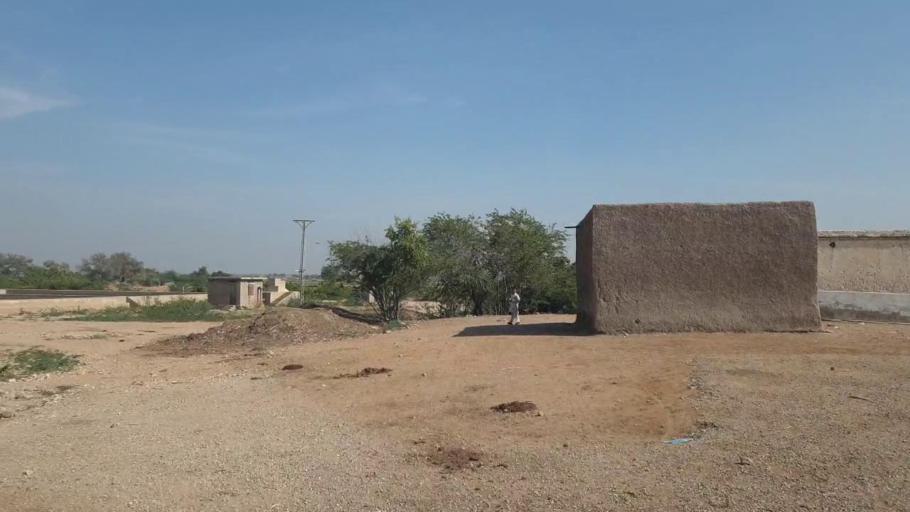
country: PK
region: Sindh
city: Matiari
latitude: 25.6798
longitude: 68.3019
